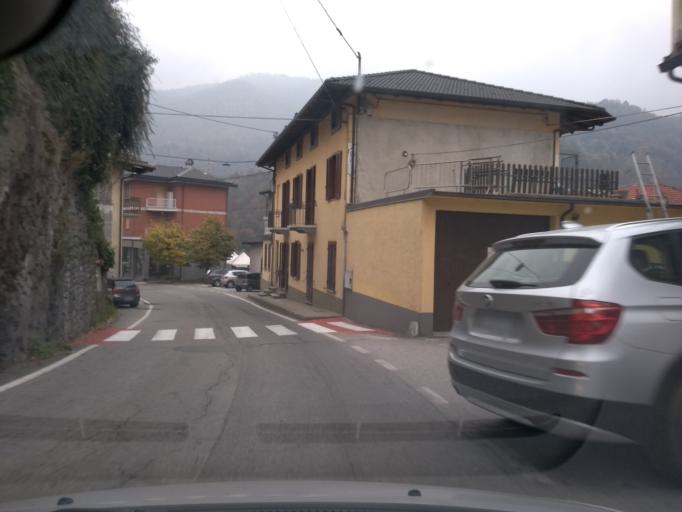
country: IT
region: Piedmont
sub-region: Provincia di Torino
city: Mezzenile
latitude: 45.2919
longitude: 7.4003
